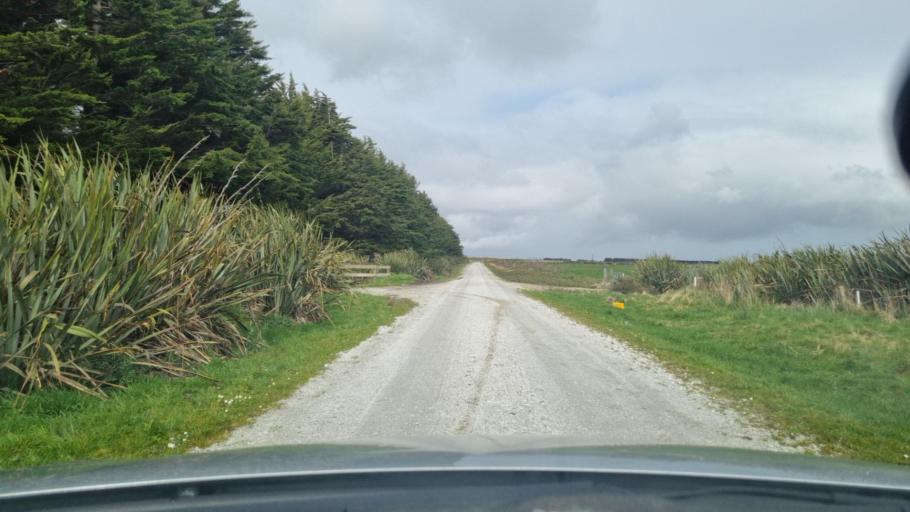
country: NZ
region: Southland
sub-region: Invercargill City
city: Bluff
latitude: -46.5160
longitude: 168.3599
